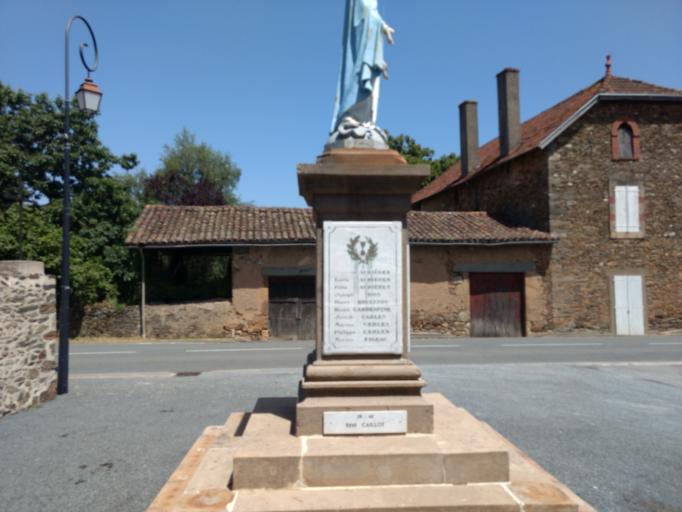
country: FR
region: Midi-Pyrenees
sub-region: Departement de l'Aveyron
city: Livinhac-le-Haut
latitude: 44.6522
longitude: 2.2539
